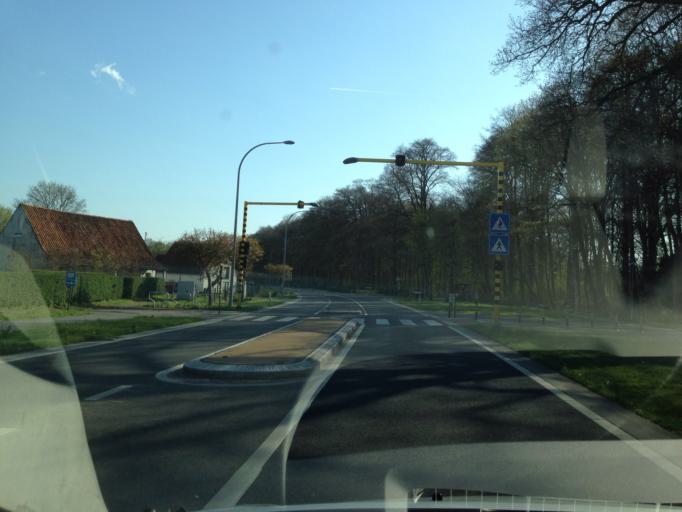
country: BE
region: Flanders
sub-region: Provincie West-Vlaanderen
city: Zedelgem
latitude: 51.1614
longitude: 3.1674
